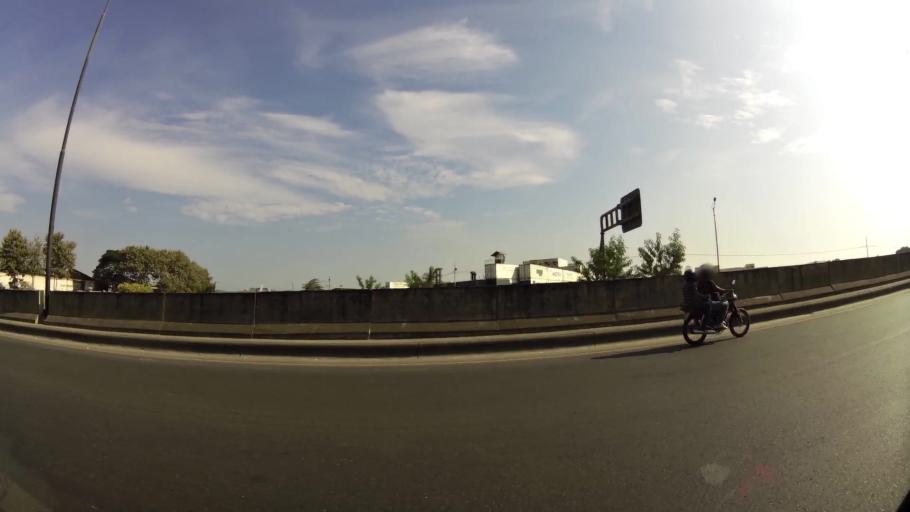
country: EC
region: Guayas
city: Santa Lucia
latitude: -2.0807
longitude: -79.9359
